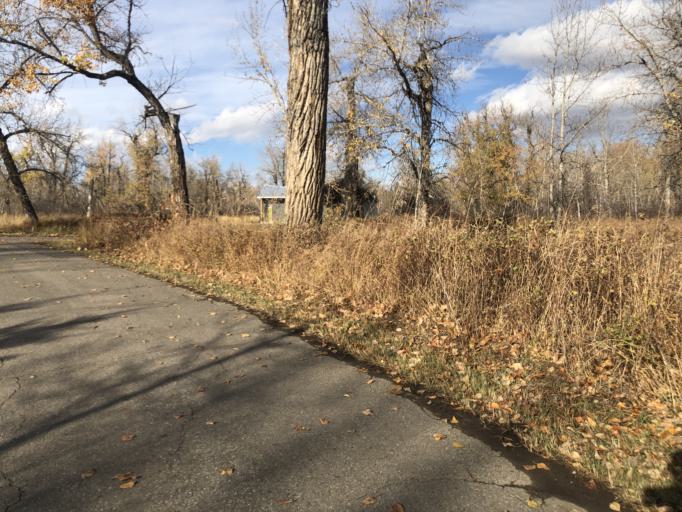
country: CA
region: Alberta
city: Calgary
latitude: 50.9264
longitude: -114.0629
